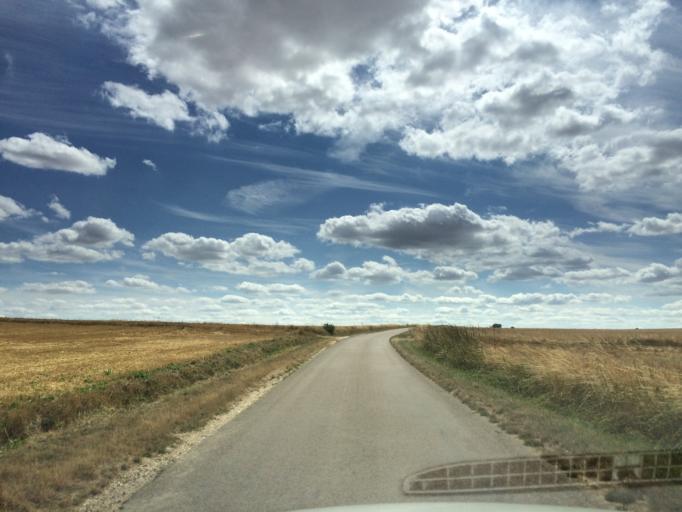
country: FR
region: Bourgogne
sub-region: Departement de l'Yonne
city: Fleury-la-Vallee
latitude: 47.8776
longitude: 3.4045
